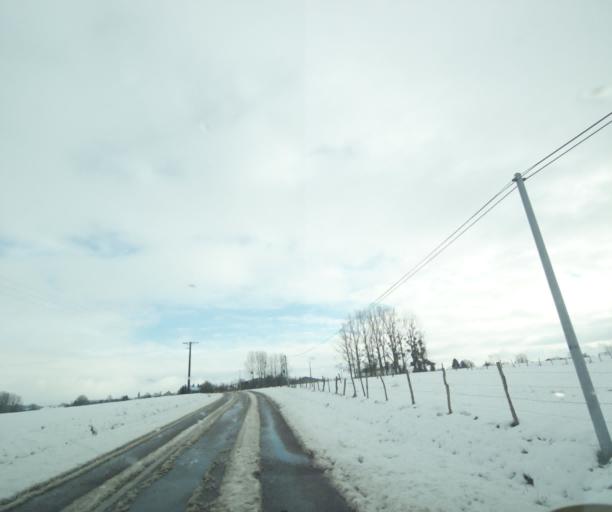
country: FR
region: Champagne-Ardenne
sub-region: Departement de la Haute-Marne
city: Montier-en-Der
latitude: 48.4539
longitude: 4.6672
